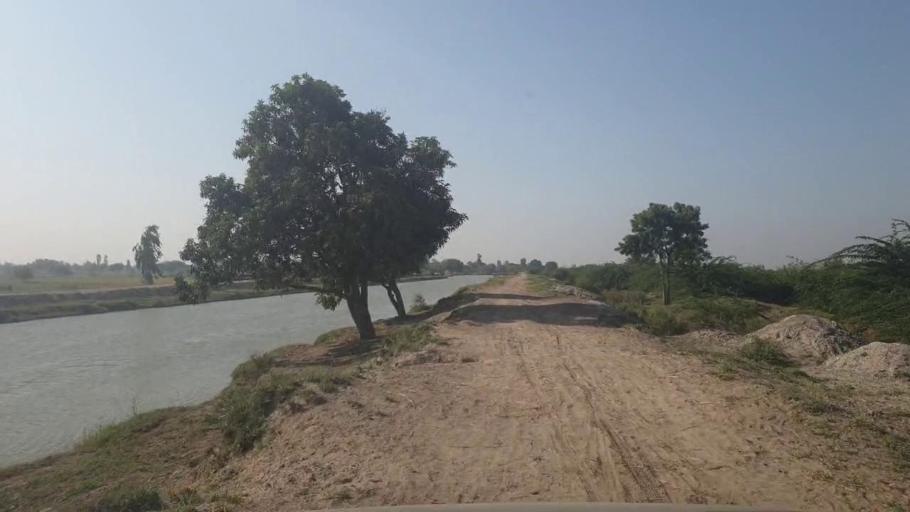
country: PK
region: Sindh
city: Badin
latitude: 24.6906
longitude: 68.8687
